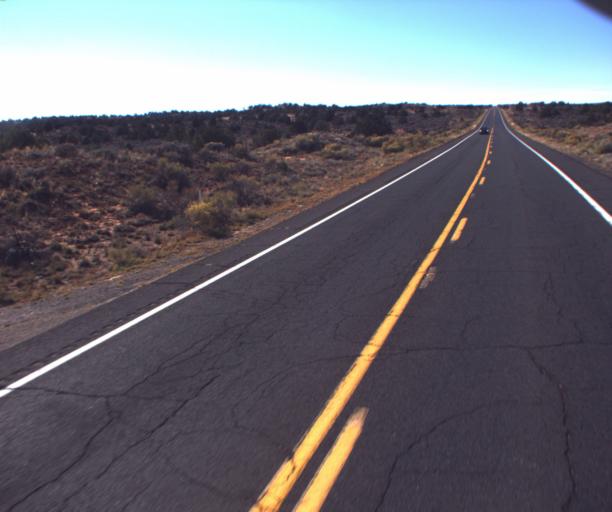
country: US
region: Arizona
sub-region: Coconino County
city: Kaibito
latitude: 36.5769
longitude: -110.7743
